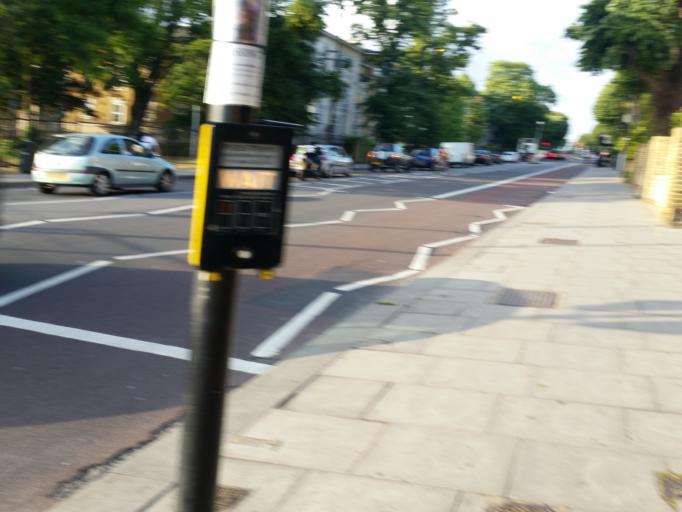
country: GB
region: England
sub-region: Greater London
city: Holloway
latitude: 51.5464
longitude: -0.1323
